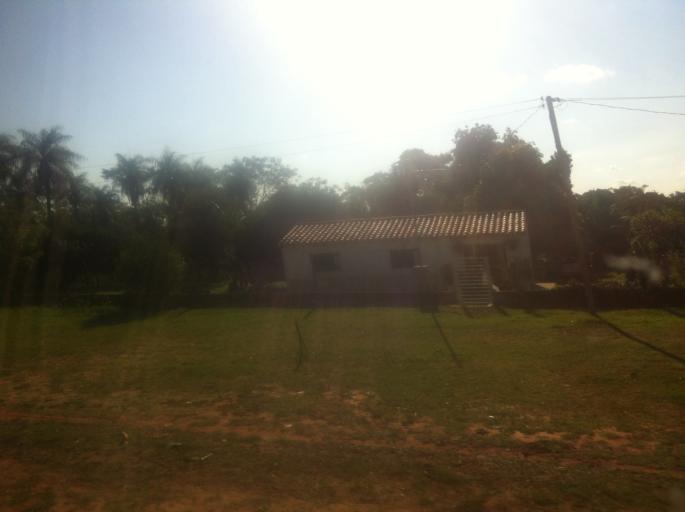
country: PY
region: Paraguari
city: Carapegua
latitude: -25.7987
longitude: -57.2620
